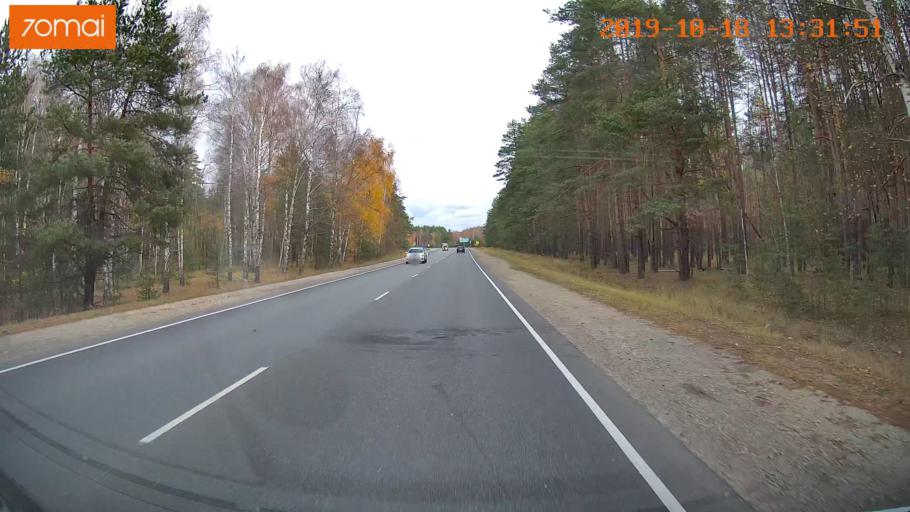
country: RU
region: Rjazan
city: Solotcha
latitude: 54.8261
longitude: 39.9085
